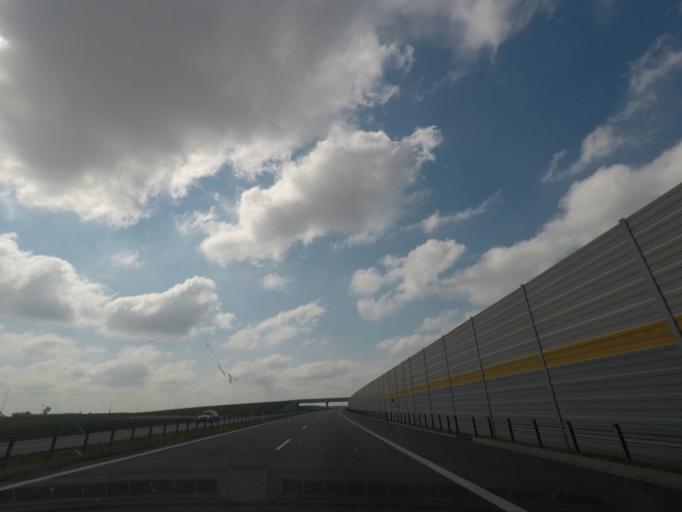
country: PL
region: Kujawsko-Pomorskie
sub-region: Powiat wabrzeski
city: Pluznica
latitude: 53.2091
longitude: 18.7395
